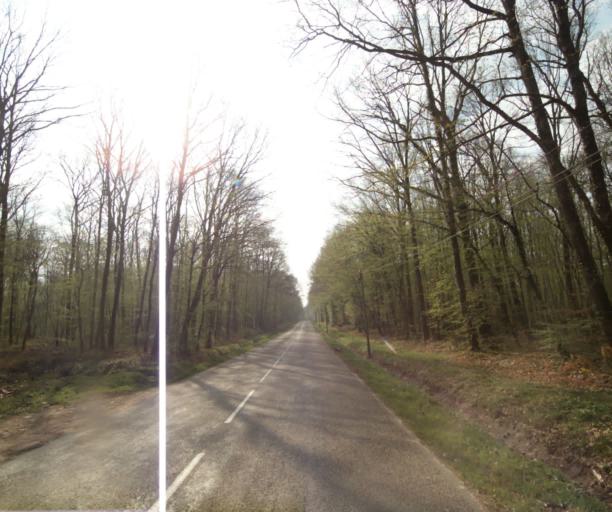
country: FR
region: Bourgogne
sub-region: Departement de Saone-et-Loire
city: Charolles
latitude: 46.4569
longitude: 4.2554
